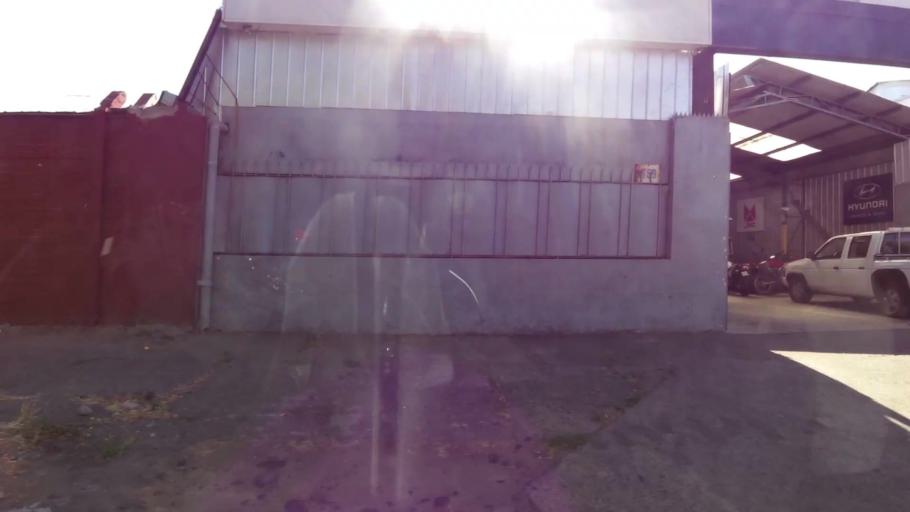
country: CL
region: Maule
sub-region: Provincia de Talca
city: Talca
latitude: -35.4187
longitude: -71.6632
